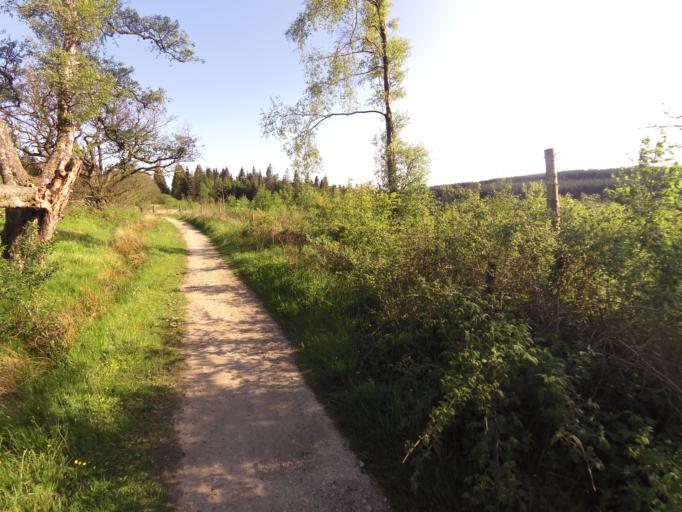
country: GB
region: England
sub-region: North Yorkshire
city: Settle
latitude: 54.0162
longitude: -2.3871
